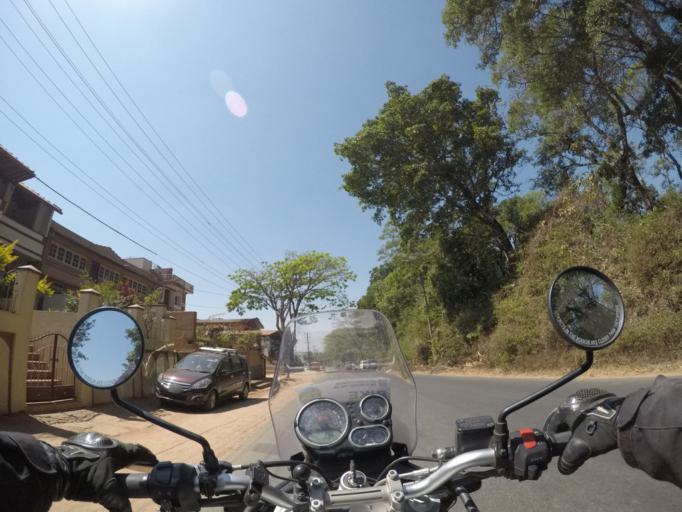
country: IN
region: Karnataka
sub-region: Hassan
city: Sakleshpur
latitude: 12.9491
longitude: 75.8054
